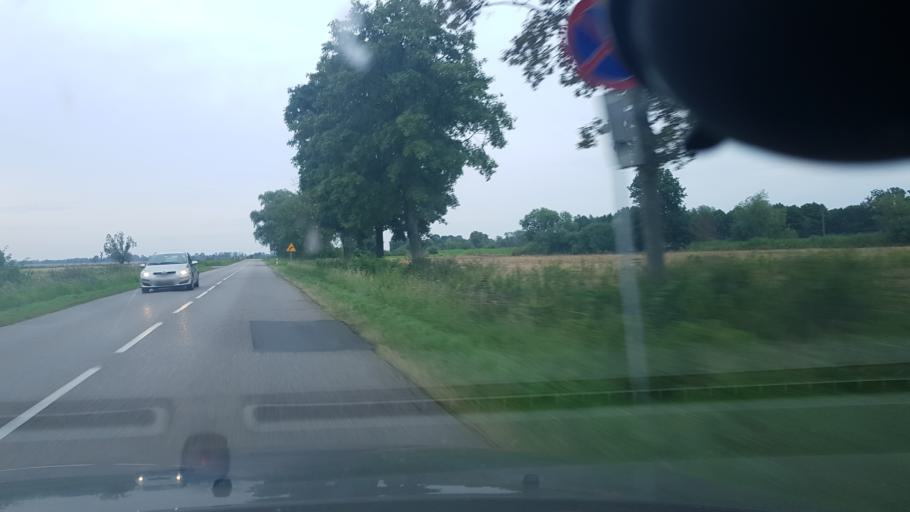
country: PL
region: Pomeranian Voivodeship
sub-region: Powiat nowodworski
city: Nowy Dwor Gdanski
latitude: 54.2355
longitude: 19.1271
